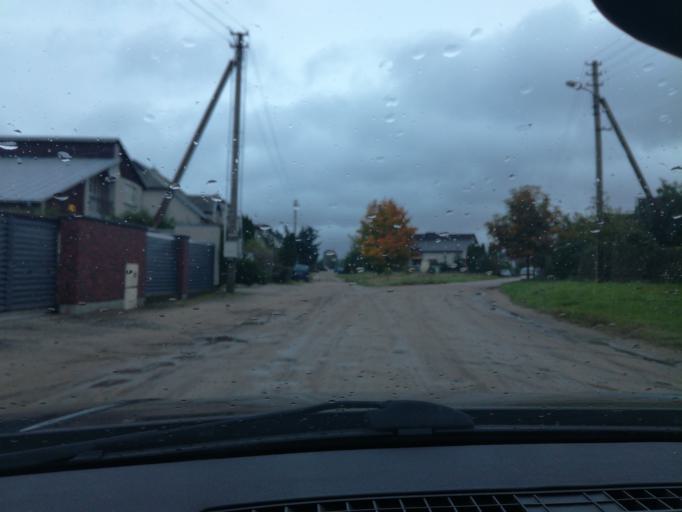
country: LT
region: Alytaus apskritis
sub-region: Alytus
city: Alytus
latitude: 54.3875
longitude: 24.0510
